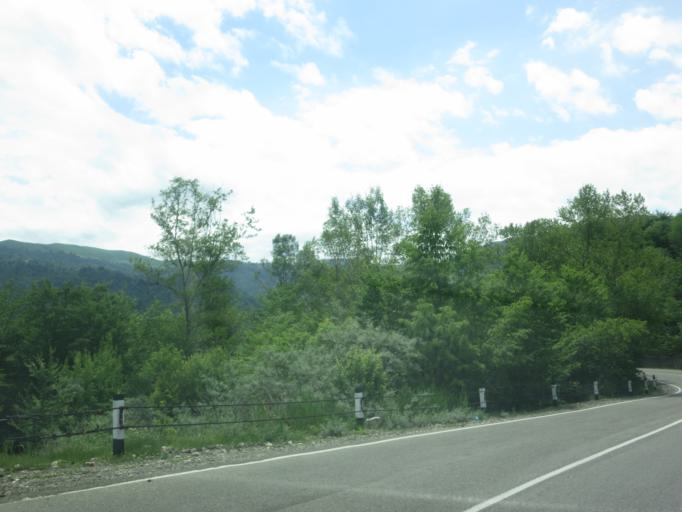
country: GE
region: Kakheti
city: Sagarejo
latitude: 41.8684
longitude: 45.3475
